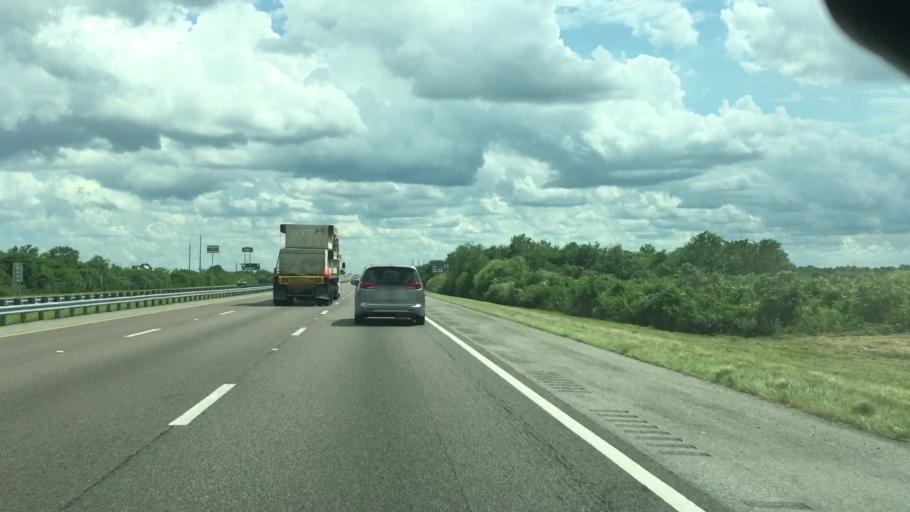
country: US
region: Florida
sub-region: Brevard County
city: Titusville
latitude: 28.5622
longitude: -80.8523
